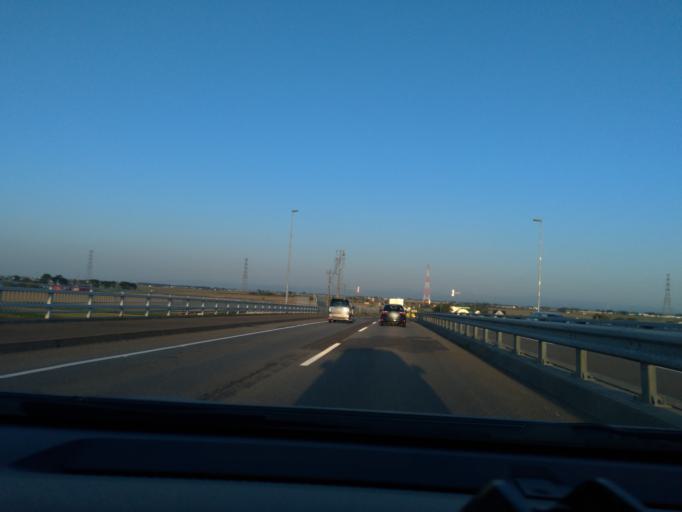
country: JP
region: Hokkaido
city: Tobetsu
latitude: 43.1816
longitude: 141.4918
